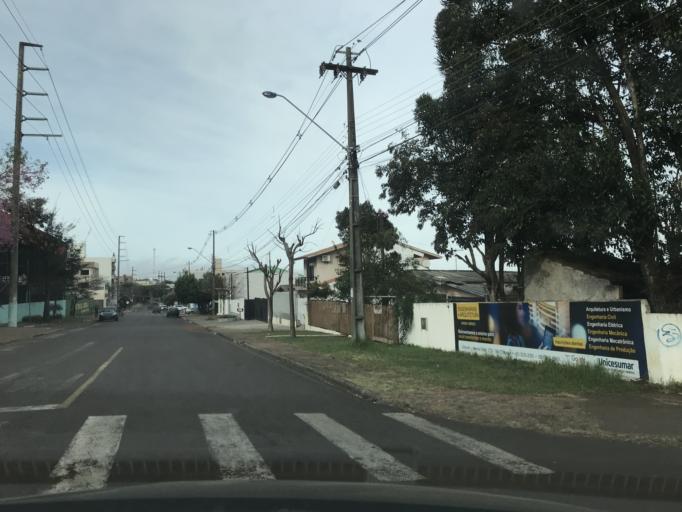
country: BR
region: Parana
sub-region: Cascavel
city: Cascavel
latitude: -24.9541
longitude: -53.4816
